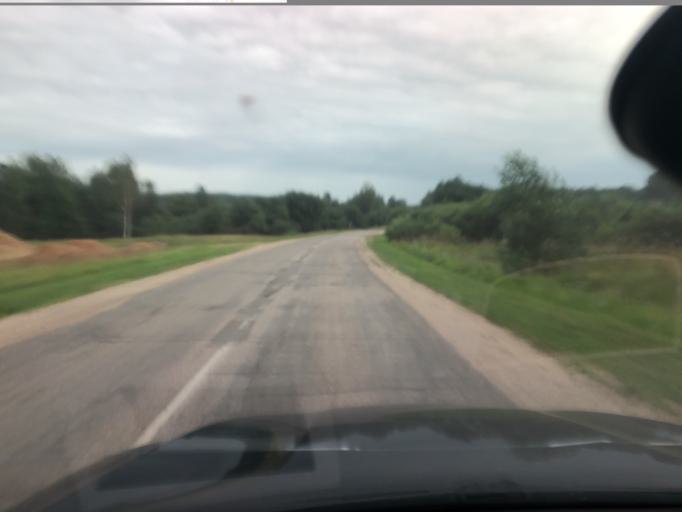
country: RU
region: Jaroslavl
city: Petrovsk
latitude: 56.9850
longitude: 39.1356
